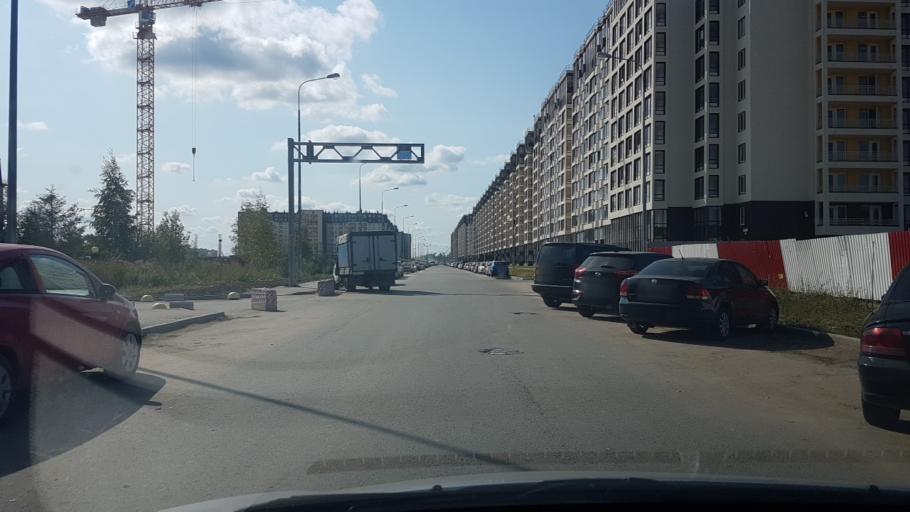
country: RU
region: St.-Petersburg
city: Sosnovaya Polyana
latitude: 59.8442
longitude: 30.1142
